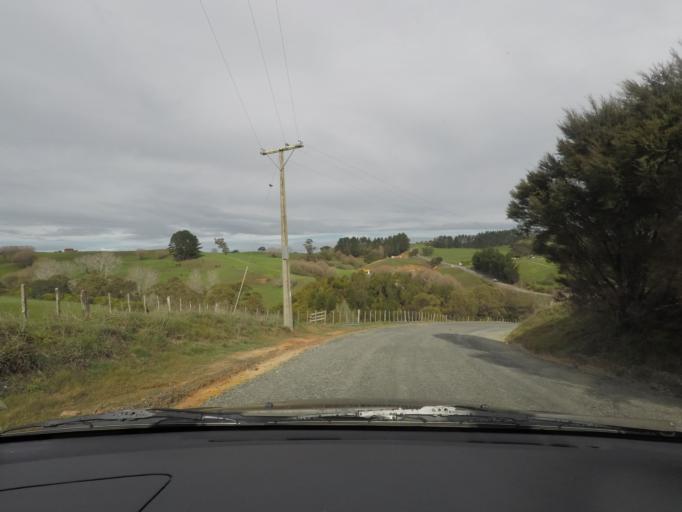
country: NZ
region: Auckland
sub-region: Auckland
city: Warkworth
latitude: -36.4478
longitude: 174.7510
